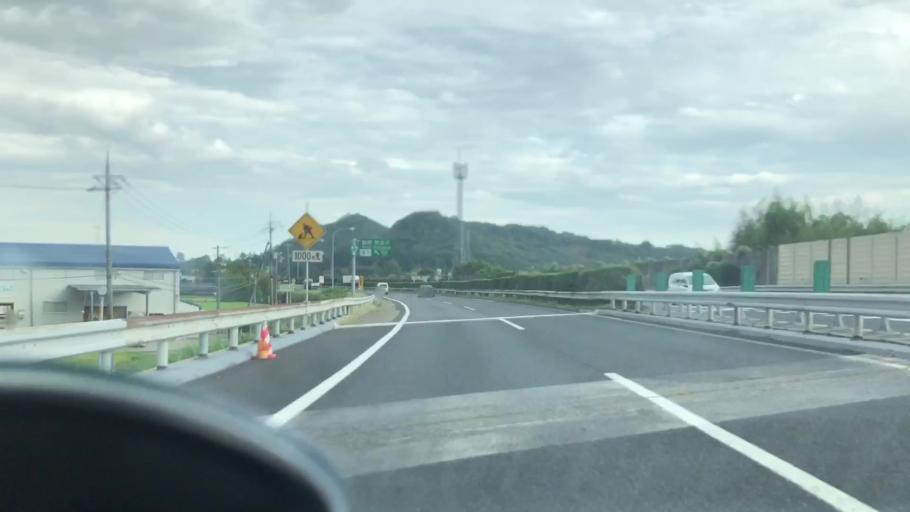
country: JP
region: Hyogo
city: Yashiro
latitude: 34.9352
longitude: 134.8607
